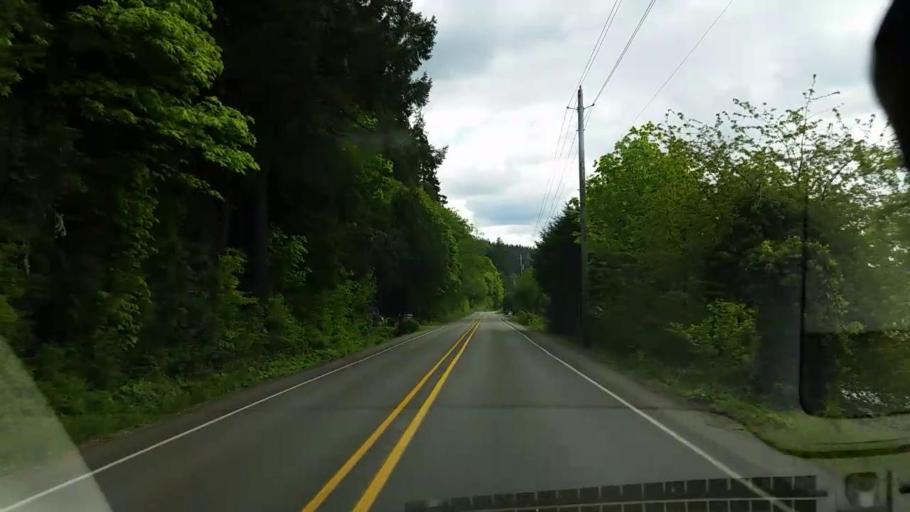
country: US
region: Washington
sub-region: Mason County
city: Shelton
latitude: 47.3467
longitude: -123.1086
